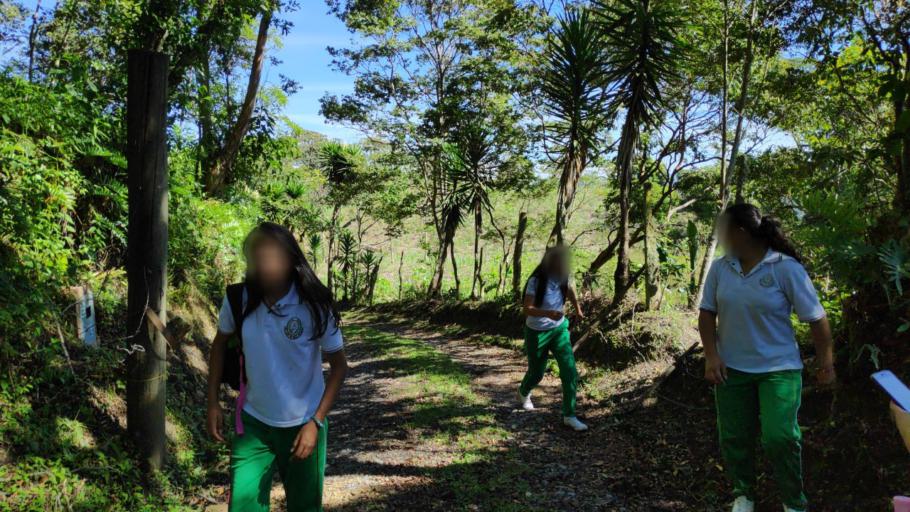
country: CO
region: Santander
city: Guepsa
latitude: 5.9876
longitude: -73.5414
